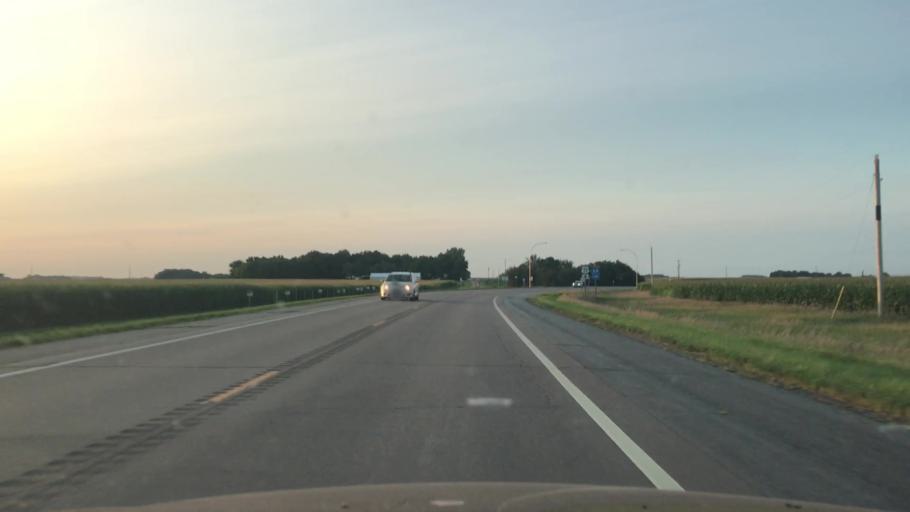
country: US
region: Minnesota
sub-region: Redwood County
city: Redwood Falls
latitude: 44.4108
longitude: -95.1276
